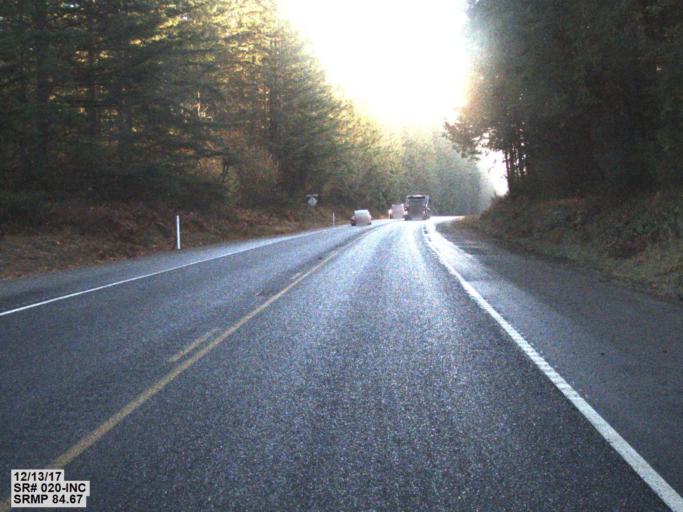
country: US
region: Washington
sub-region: Snohomish County
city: Darrington
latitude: 48.5410
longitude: -121.8377
